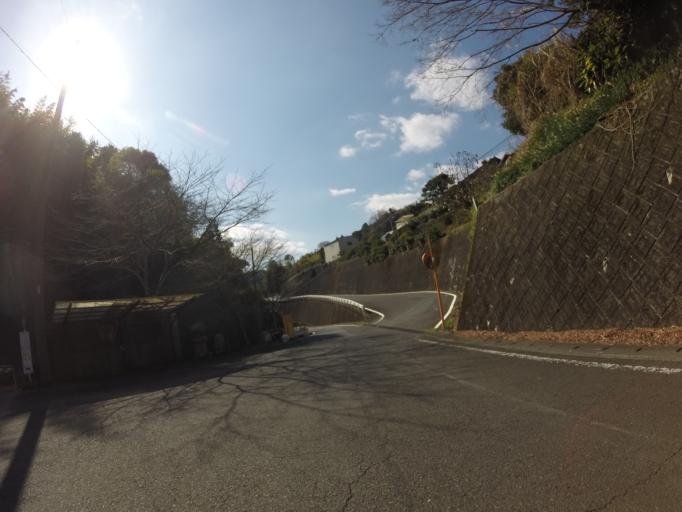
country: JP
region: Shizuoka
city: Shizuoka-shi
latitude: 35.0750
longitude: 138.4942
